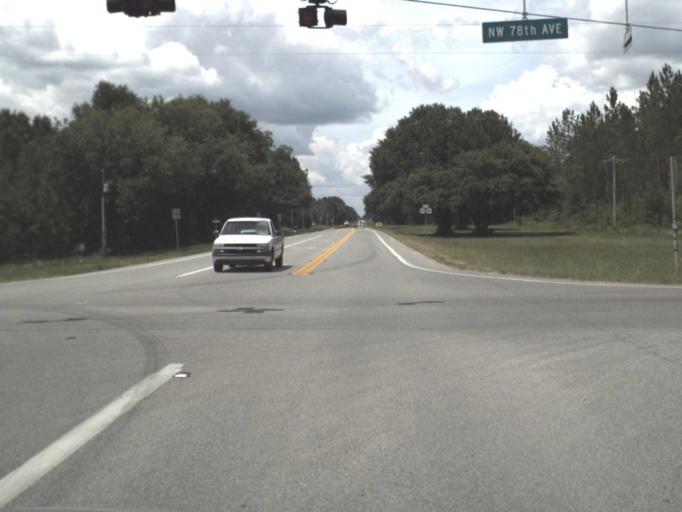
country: US
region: Florida
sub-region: Alachua County
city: Newberry
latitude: 29.7273
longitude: -82.6071
